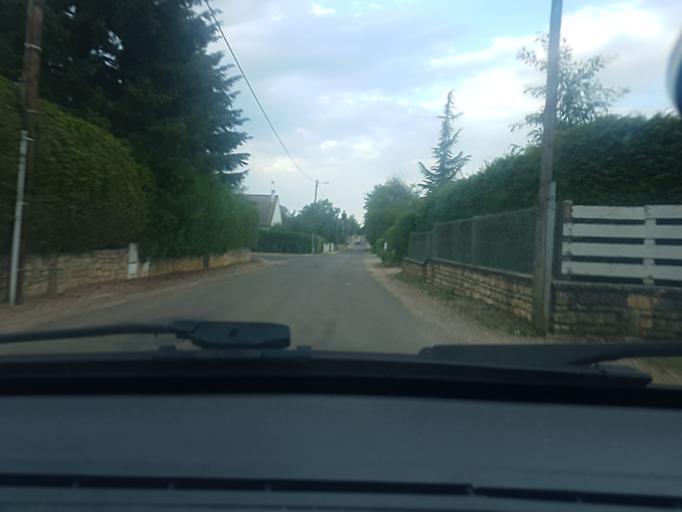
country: FR
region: Bourgogne
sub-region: Departement de Saone-et-Loire
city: Givry
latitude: 46.7763
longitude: 4.7431
